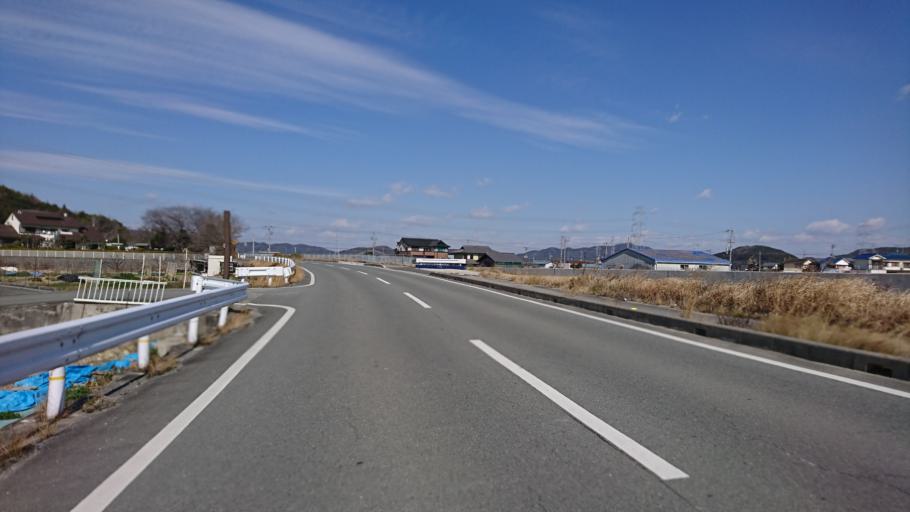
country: JP
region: Hyogo
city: Kakogawacho-honmachi
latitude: 34.7977
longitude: 134.8112
